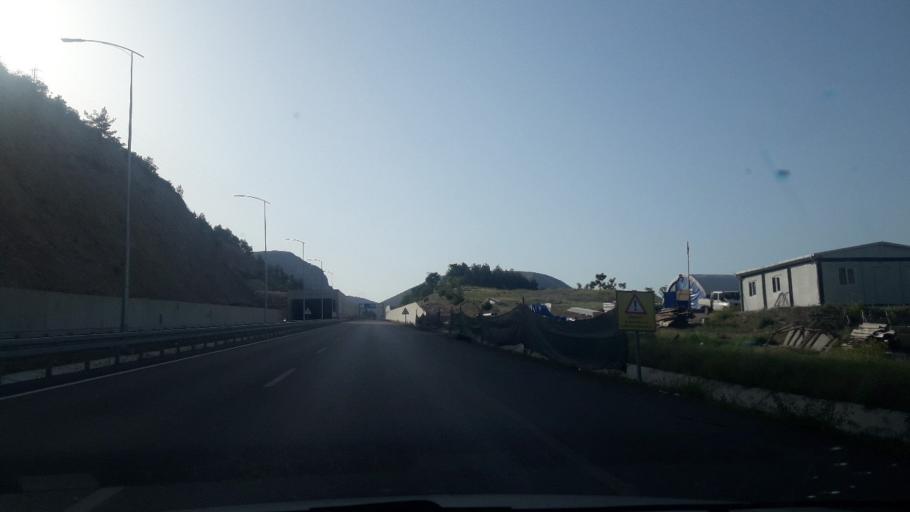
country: TR
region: Amasya
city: Amasya
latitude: 40.6412
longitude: 35.7964
